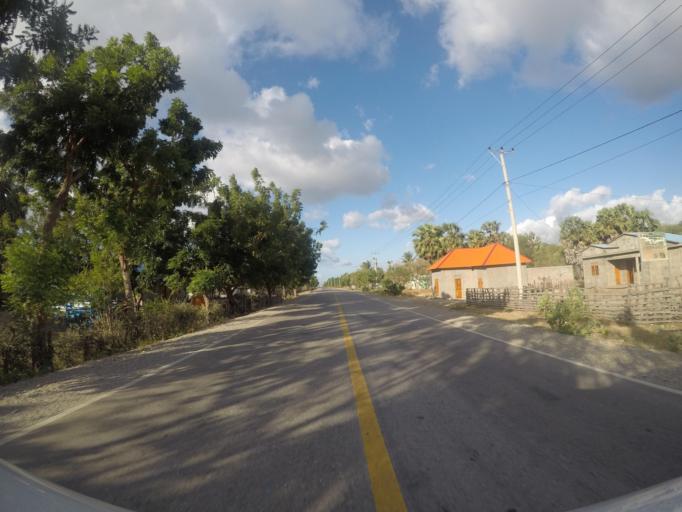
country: TL
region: Lautem
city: Lospalos
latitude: -8.3768
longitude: 126.8707
